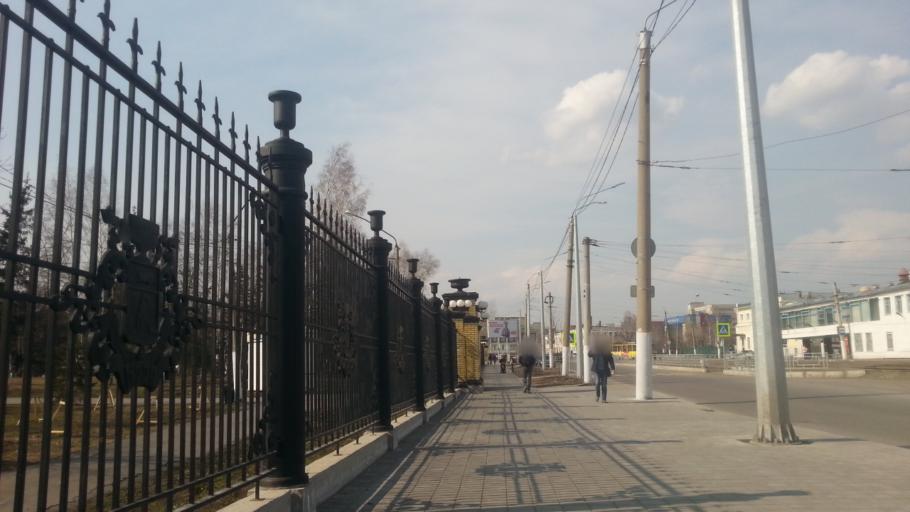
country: RU
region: Altai Krai
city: Zaton
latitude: 53.3291
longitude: 83.7908
